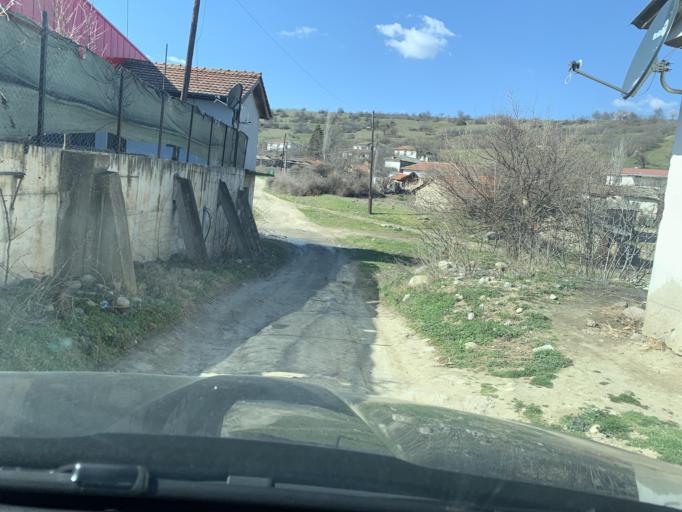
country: MK
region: Demir Kapija
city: Demir Kapija
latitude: 41.4200
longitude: 22.1663
